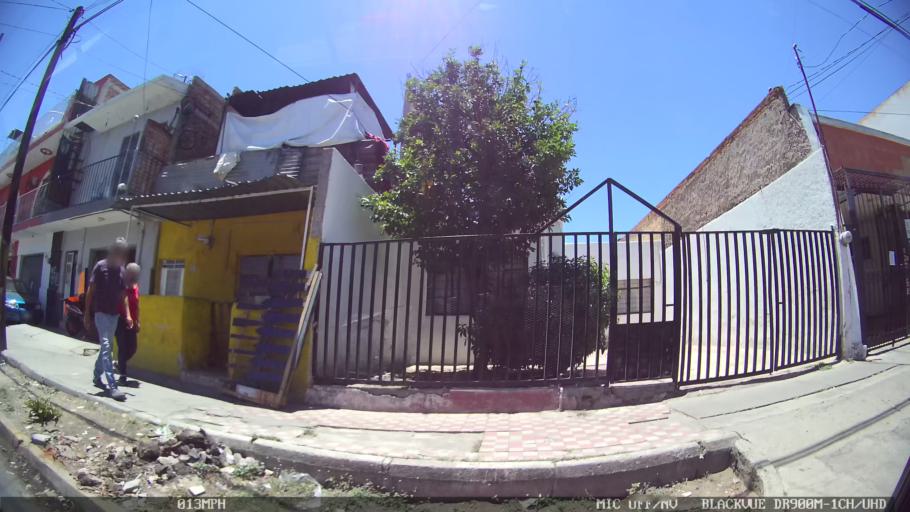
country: MX
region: Jalisco
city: Tlaquepaque
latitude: 20.6614
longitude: -103.2895
